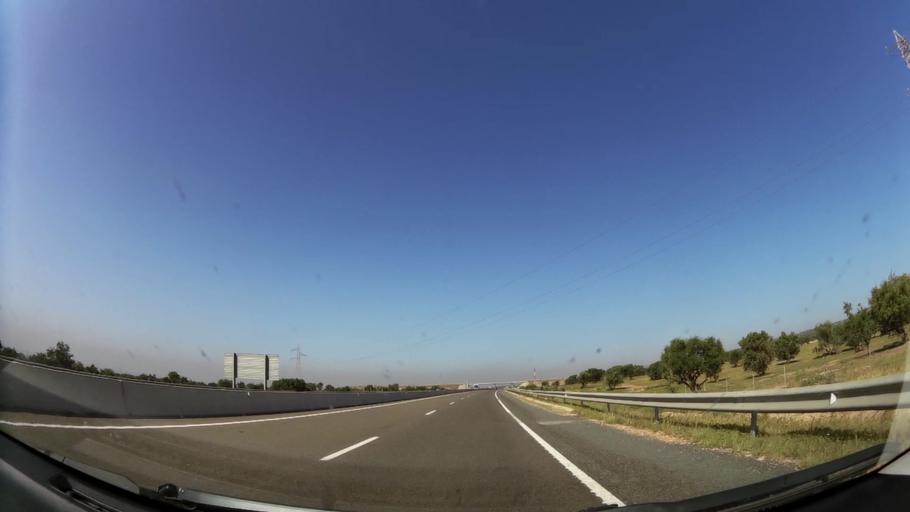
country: MA
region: Souss-Massa-Draa
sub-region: Inezgane-Ait Mellou
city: Inezgane
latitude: 30.4253
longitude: -9.3821
